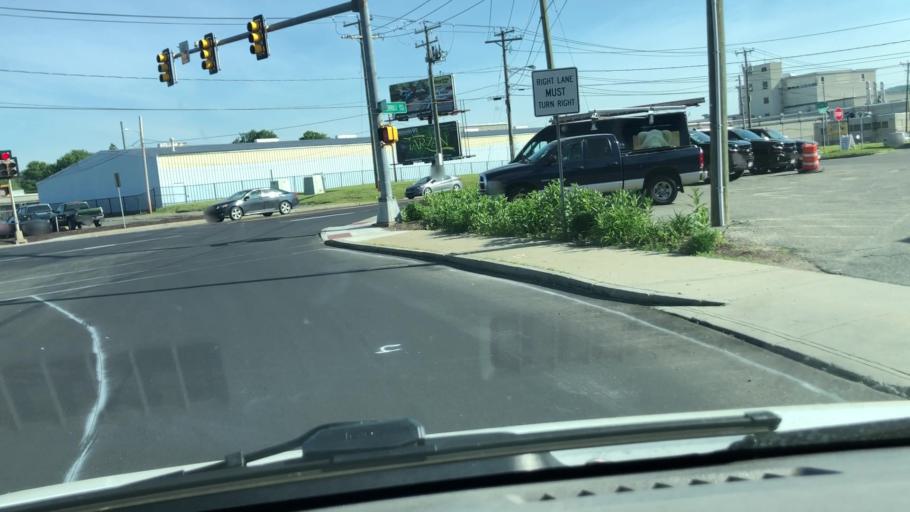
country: US
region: Massachusetts
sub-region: Berkshire County
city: Pittsfield
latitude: 42.4560
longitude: -73.2132
